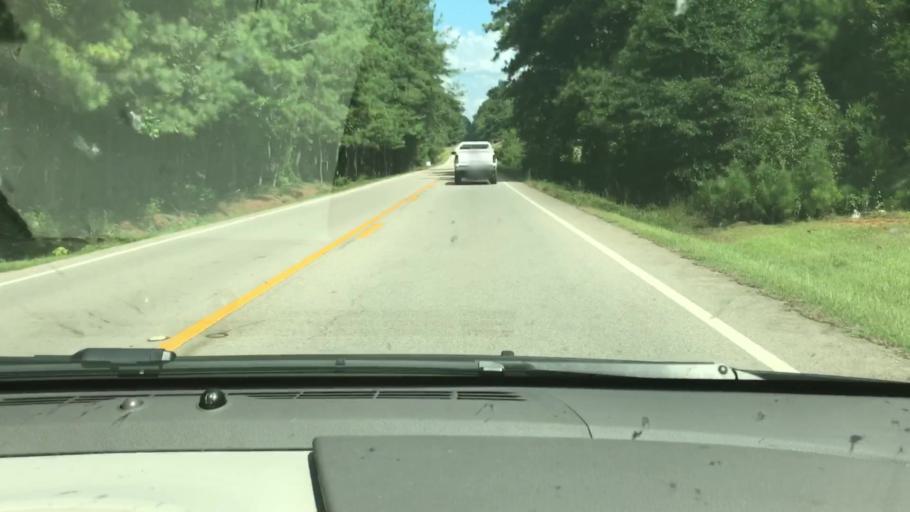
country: US
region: Georgia
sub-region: Troup County
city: La Grange
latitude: 32.9573
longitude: -85.0204
